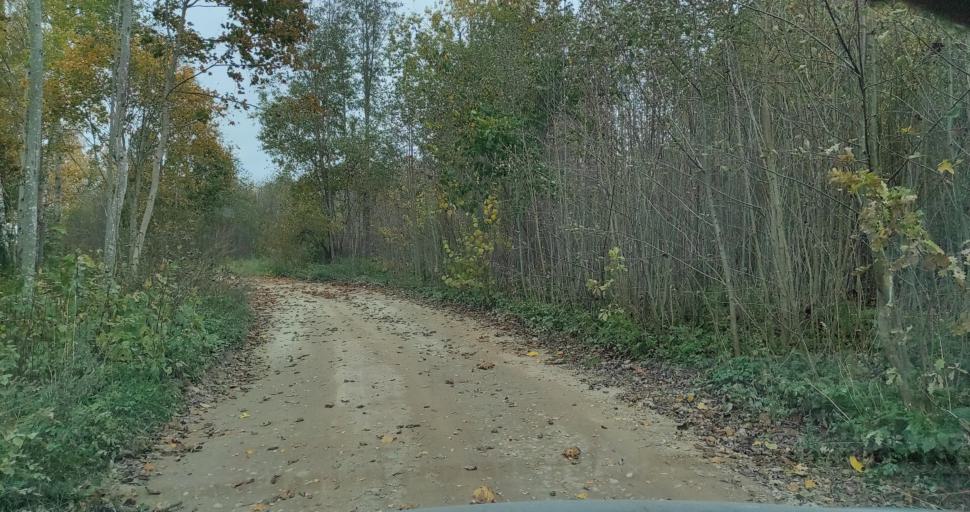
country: LV
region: Alsunga
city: Alsunga
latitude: 57.0364
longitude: 21.7123
